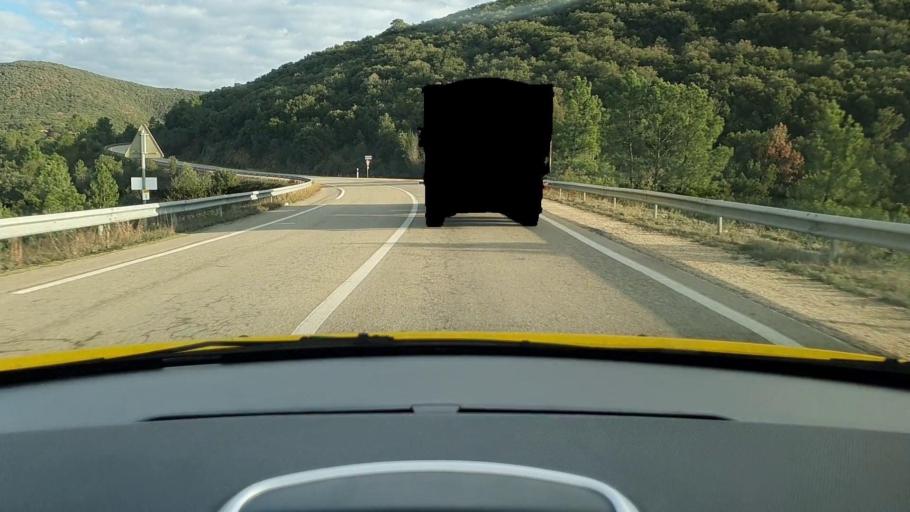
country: FR
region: Languedoc-Roussillon
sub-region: Departement du Gard
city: Laval-Pradel
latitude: 44.1963
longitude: 4.0848
